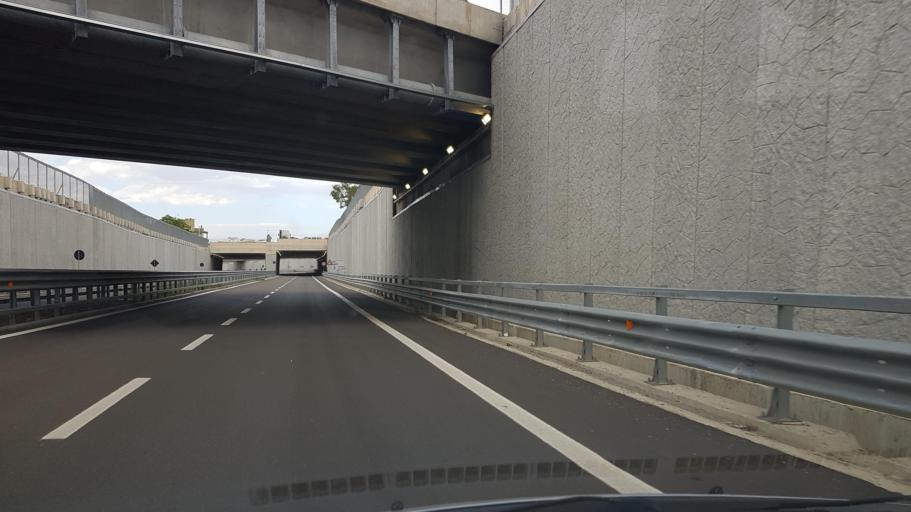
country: IT
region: Apulia
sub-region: Provincia di Taranto
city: Taranto
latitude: 40.4597
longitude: 17.2868
